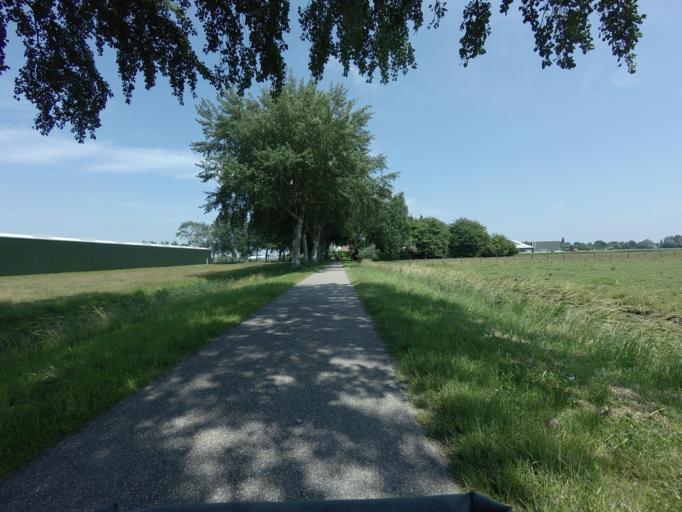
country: NL
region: North Holland
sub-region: Gemeente Opmeer
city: Opmeer
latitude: 52.6196
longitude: 4.9373
